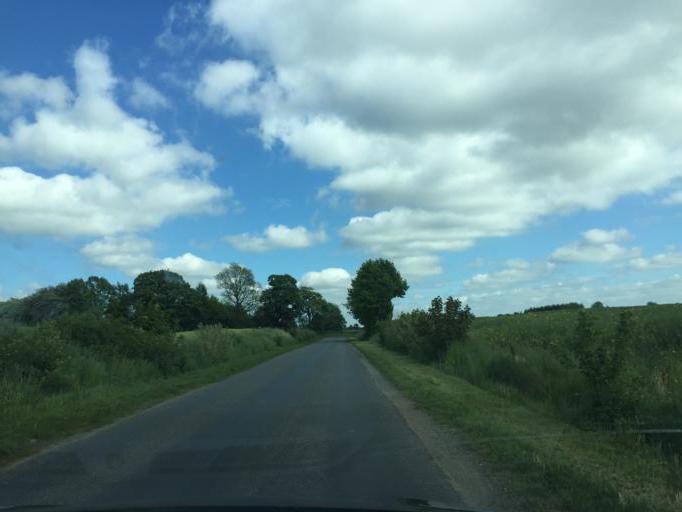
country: DK
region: South Denmark
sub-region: Assens Kommune
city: Tommerup
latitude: 55.3434
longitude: 10.2234
